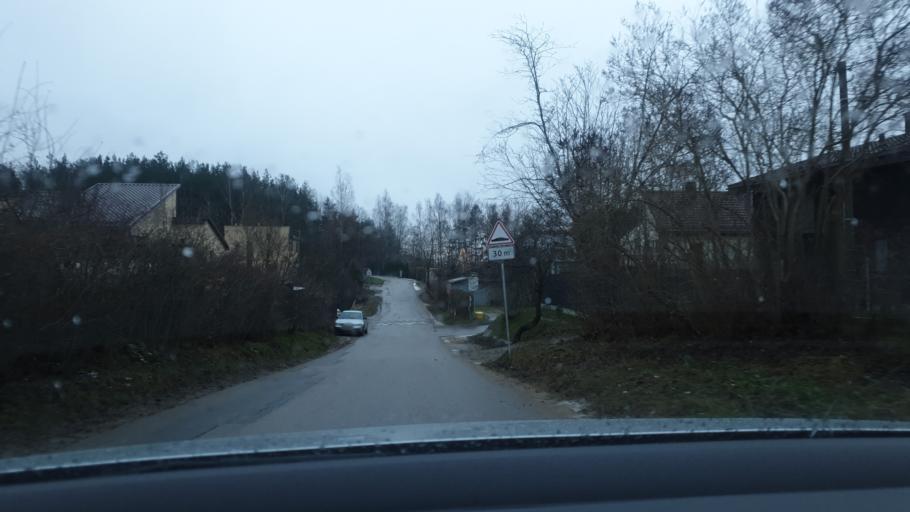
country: LT
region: Vilnius County
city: Rasos
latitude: 54.7201
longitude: 25.3868
